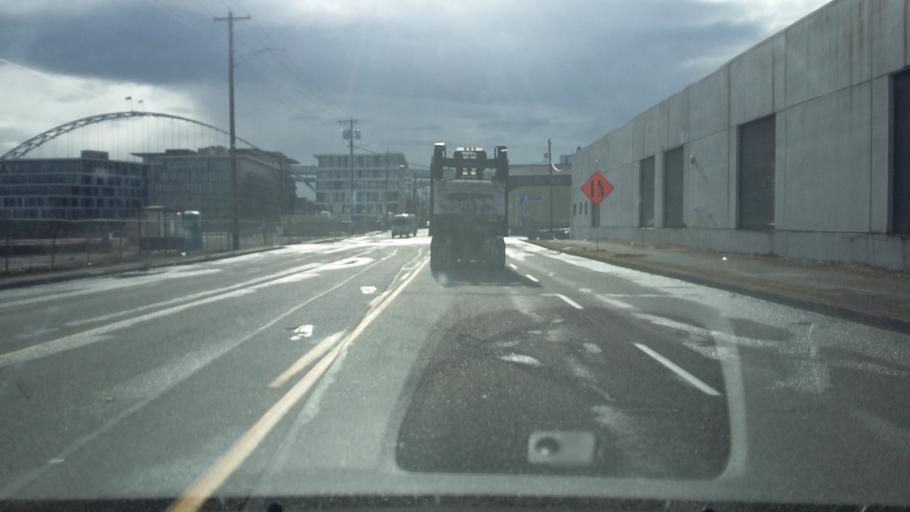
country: US
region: Oregon
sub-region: Multnomah County
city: Portland
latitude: 45.5405
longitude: -122.6928
